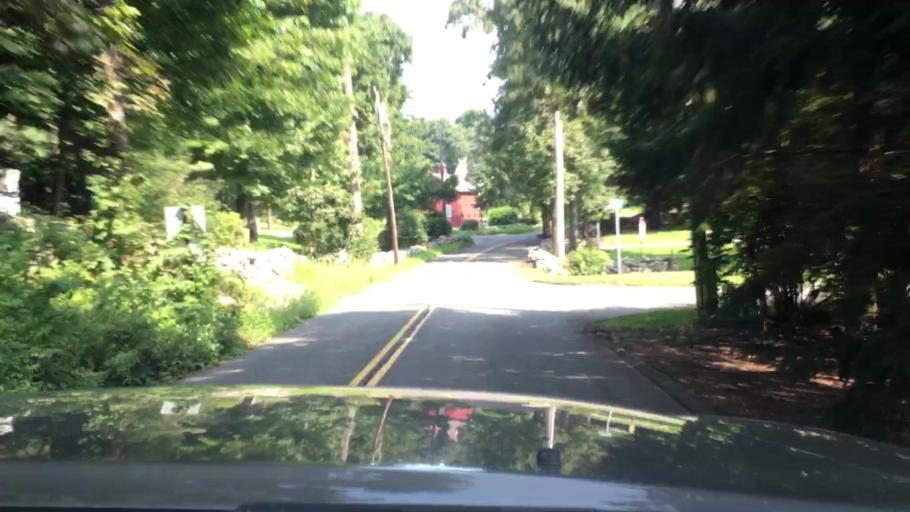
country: US
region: Connecticut
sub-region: Fairfield County
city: Georgetown
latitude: 41.2594
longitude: -73.4563
